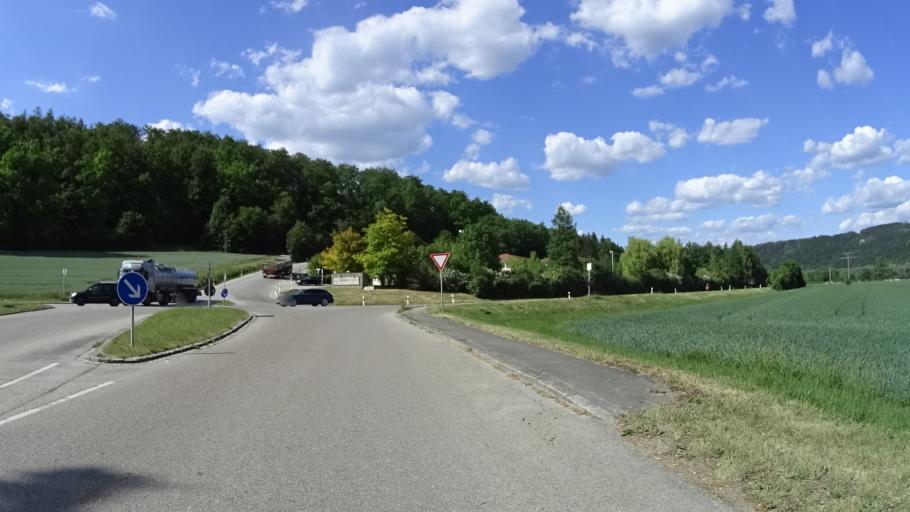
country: DE
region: Bavaria
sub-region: Upper Bavaria
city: Denkendorf
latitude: 48.9963
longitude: 11.4360
